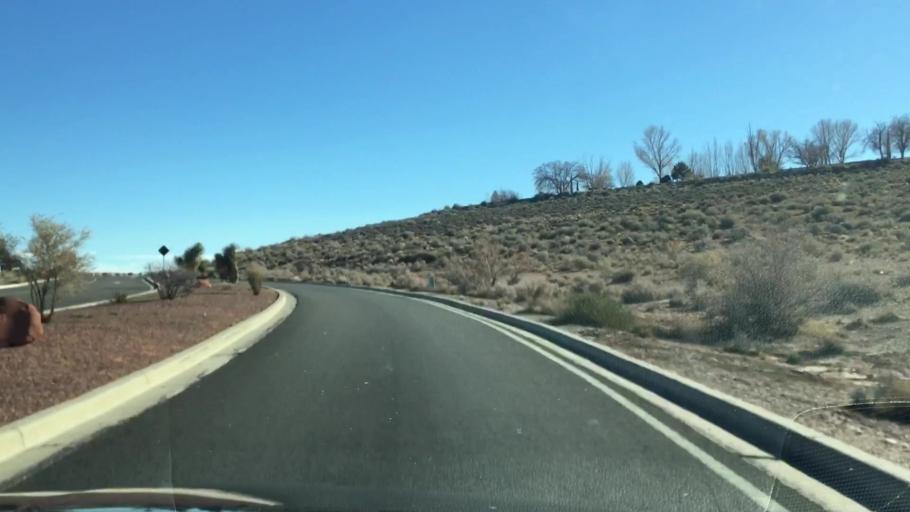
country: US
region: Arizona
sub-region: Coconino County
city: Page
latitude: 36.9945
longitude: -111.4927
